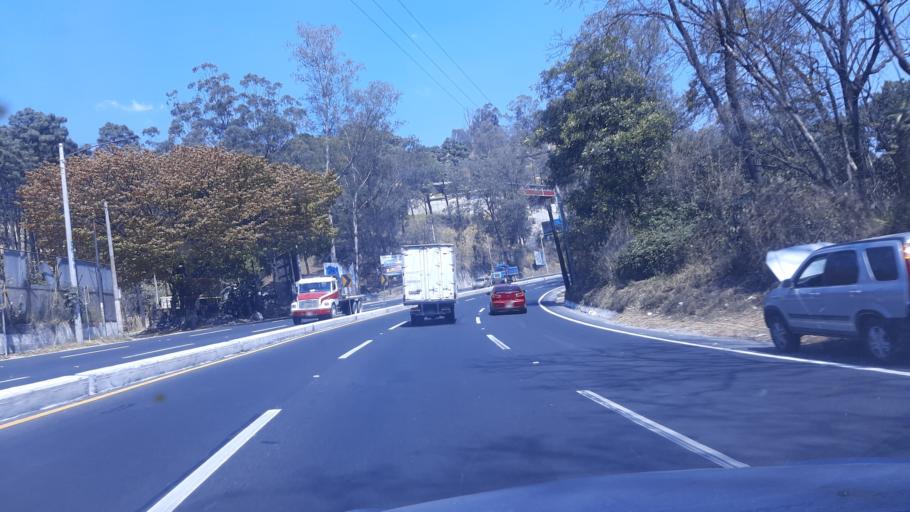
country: GT
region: Guatemala
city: Amatitlan
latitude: 14.4944
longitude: -90.6287
